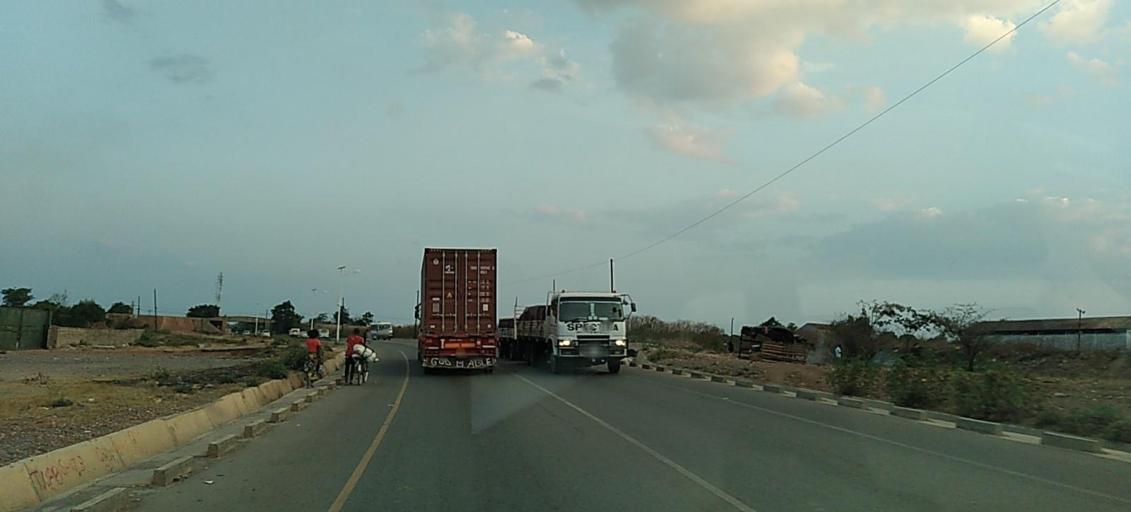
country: ZM
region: Copperbelt
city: Chingola
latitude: -12.5386
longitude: 27.8400
